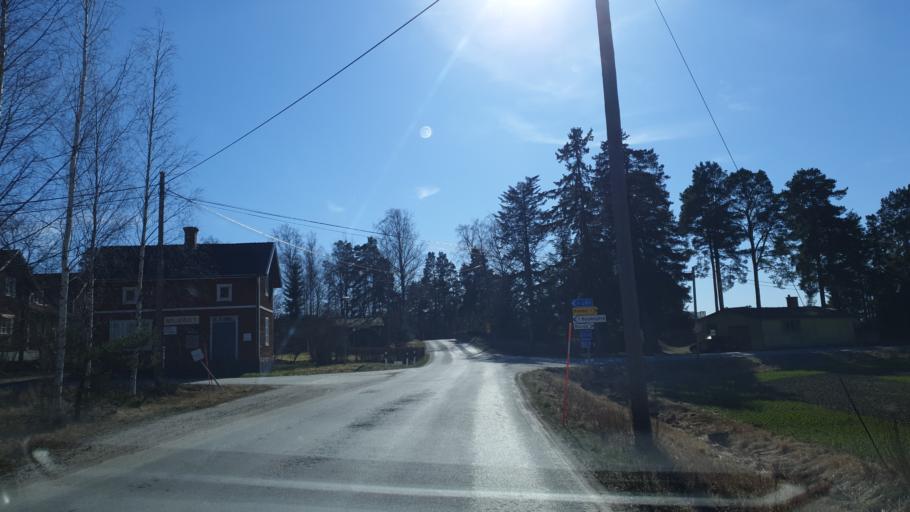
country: SE
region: Uppsala
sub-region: Enkopings Kommun
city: Dalby
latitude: 59.5662
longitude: 17.3069
